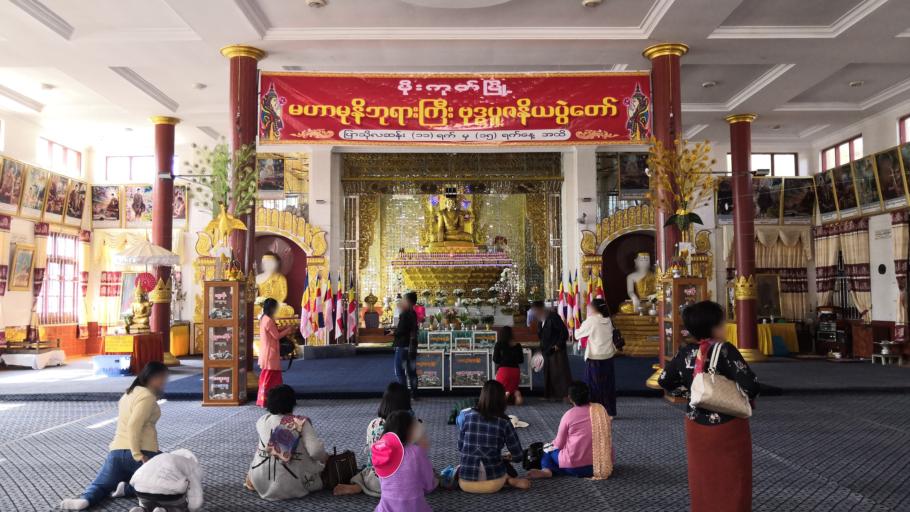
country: MM
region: Mandalay
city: Mogok
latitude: 22.9274
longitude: 96.5104
